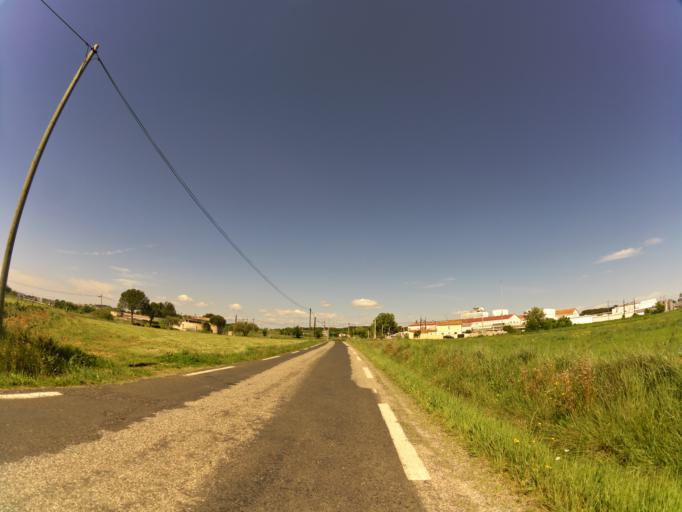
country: FR
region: Languedoc-Roussillon
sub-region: Departement du Gard
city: Mus
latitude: 43.7255
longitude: 4.1946
